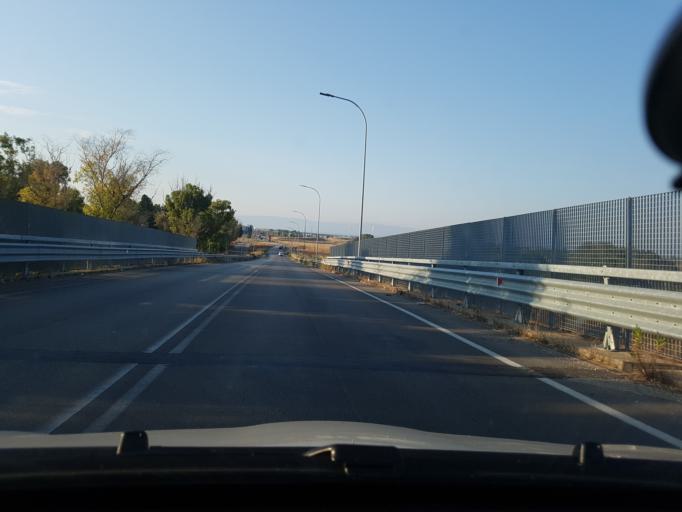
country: IT
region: Apulia
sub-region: Provincia di Foggia
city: Carapelle
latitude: 41.4074
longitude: 15.6531
